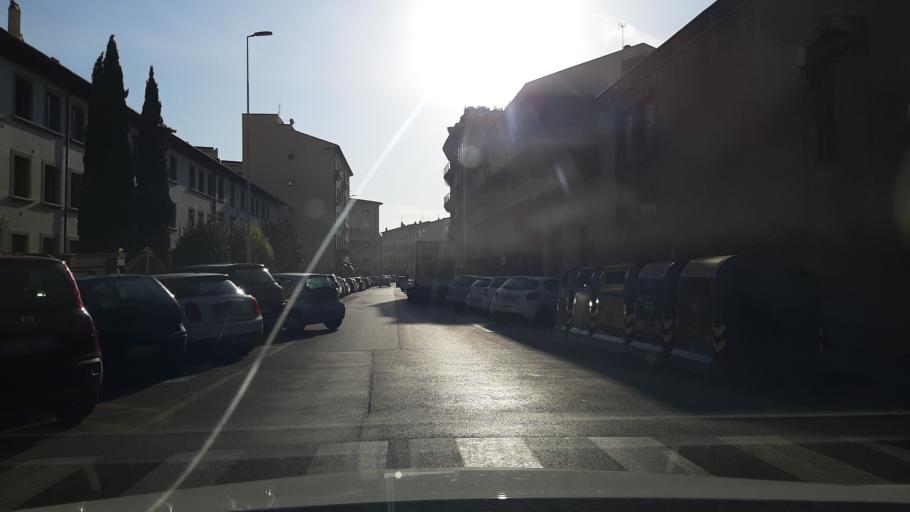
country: IT
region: Tuscany
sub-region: Province of Florence
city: Fiesole
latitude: 43.7839
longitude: 11.2832
